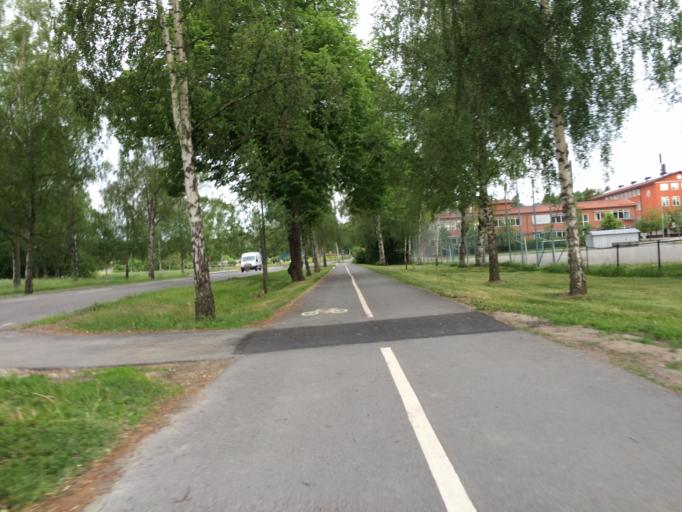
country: SE
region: Stockholm
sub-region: Danderyds Kommun
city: Djursholm
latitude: 59.3983
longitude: 18.0802
